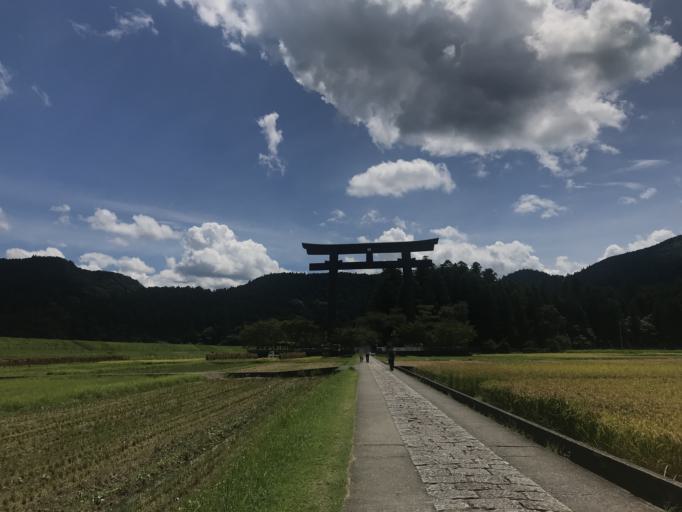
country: JP
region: Wakayama
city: Shingu
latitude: 33.8374
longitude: 135.7756
